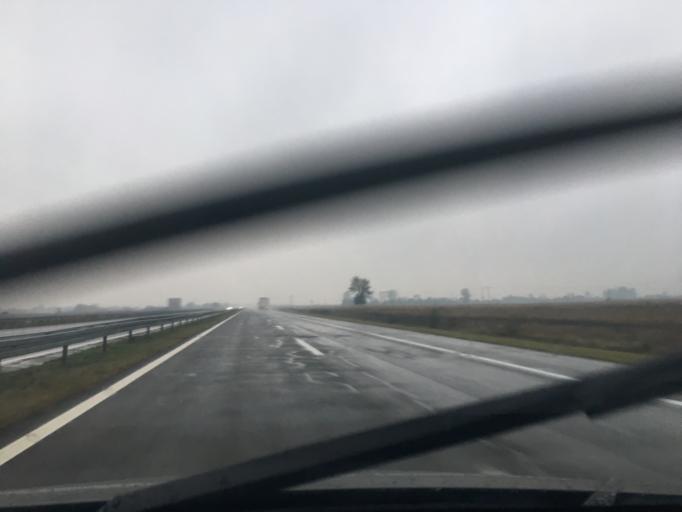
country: RS
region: Central Serbia
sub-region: Nisavski Okrug
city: Doljevac
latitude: 43.1254
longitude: 21.9120
